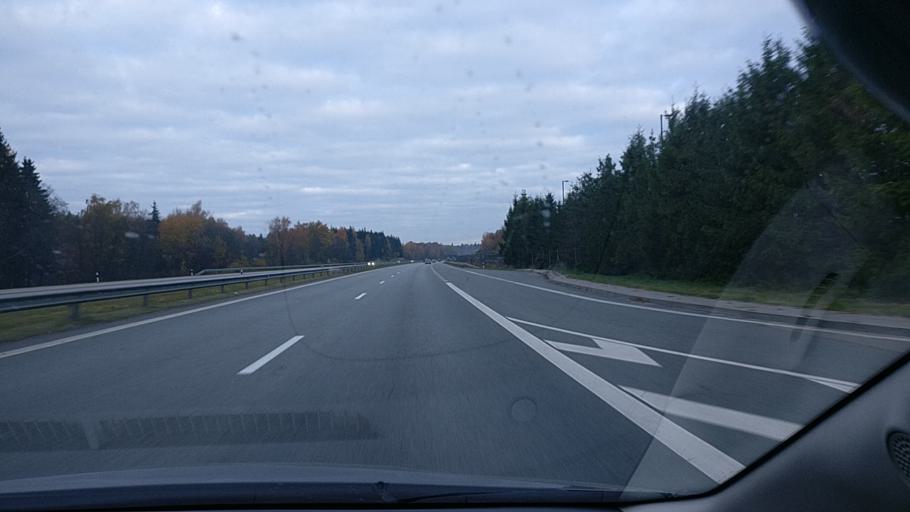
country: LT
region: Vilnius County
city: Pasilaiciai
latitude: 54.8271
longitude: 25.1294
